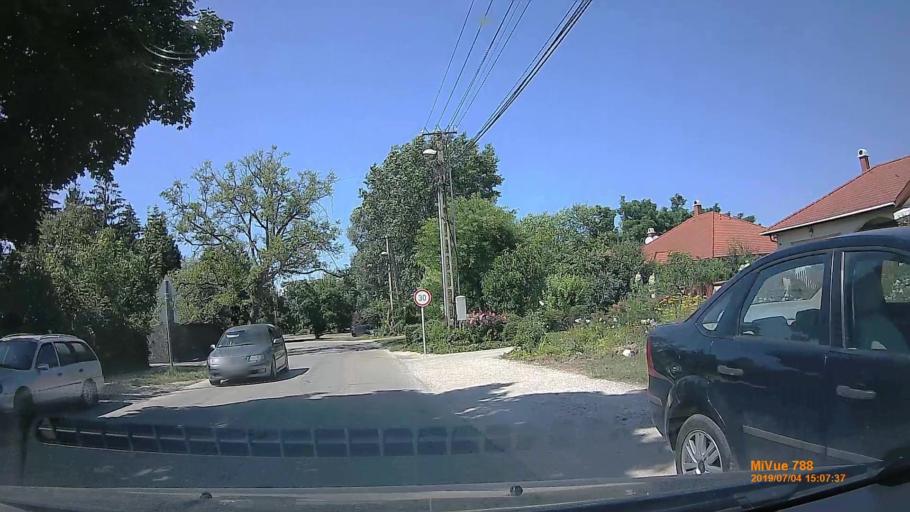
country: HU
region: Komarom-Esztergom
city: Tatabanya
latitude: 47.5742
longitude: 18.3915
